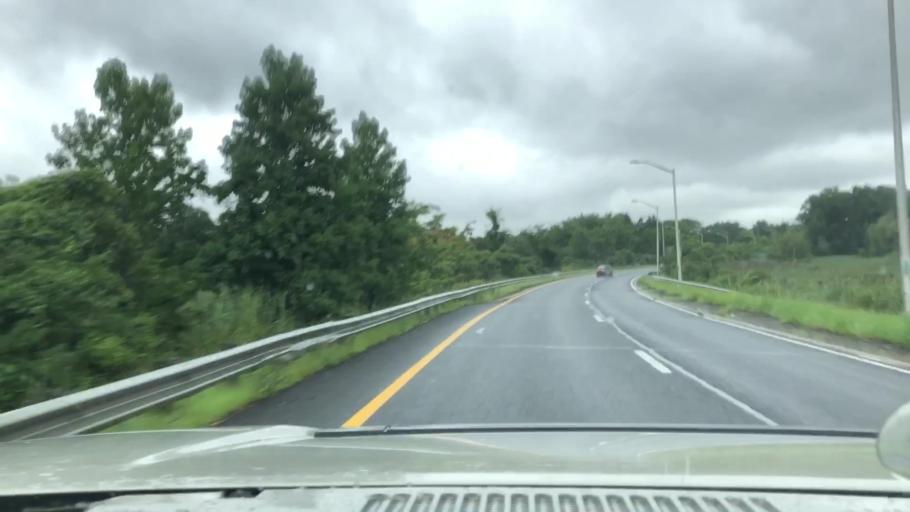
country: US
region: New York
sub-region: Richmond County
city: Bloomfield
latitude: 40.6197
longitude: -74.1752
